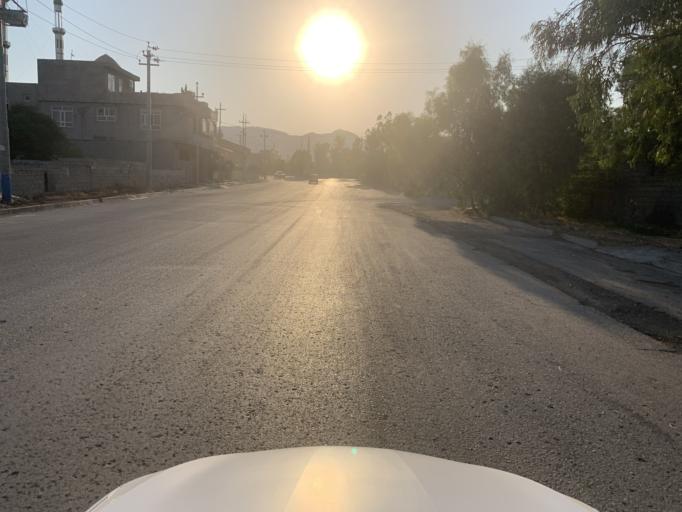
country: IQ
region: As Sulaymaniyah
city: Raniye
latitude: 36.2456
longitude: 44.8835
